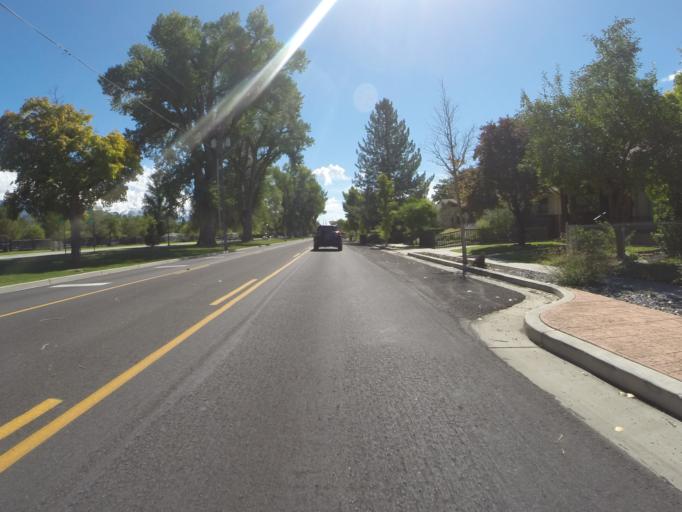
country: US
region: Utah
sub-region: Salt Lake County
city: Salt Lake City
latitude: 40.7463
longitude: -111.8768
